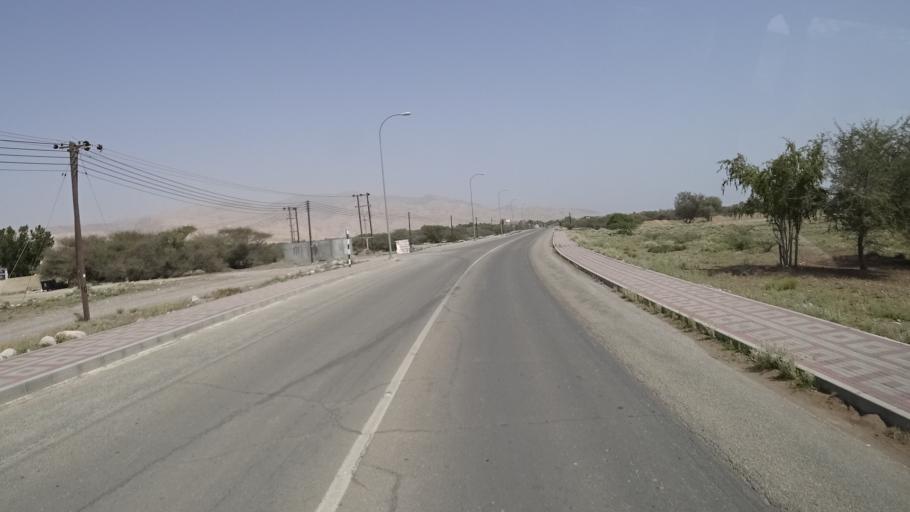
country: OM
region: Muhafazat Masqat
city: Muscat
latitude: 23.2283
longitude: 58.9118
